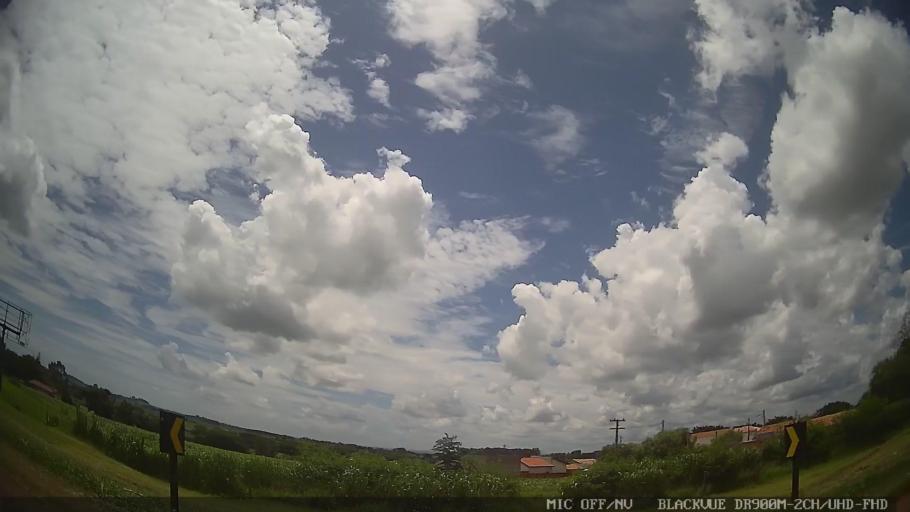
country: BR
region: Sao Paulo
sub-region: Laranjal Paulista
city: Laranjal Paulista
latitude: -23.0363
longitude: -47.8850
